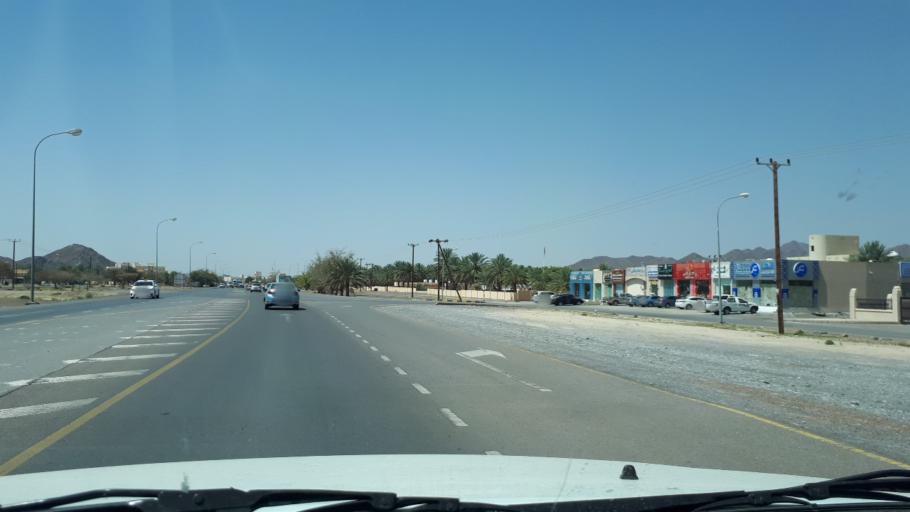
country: OM
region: Muhafazat ad Dakhiliyah
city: Bahla'
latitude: 22.9926
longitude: 57.3131
